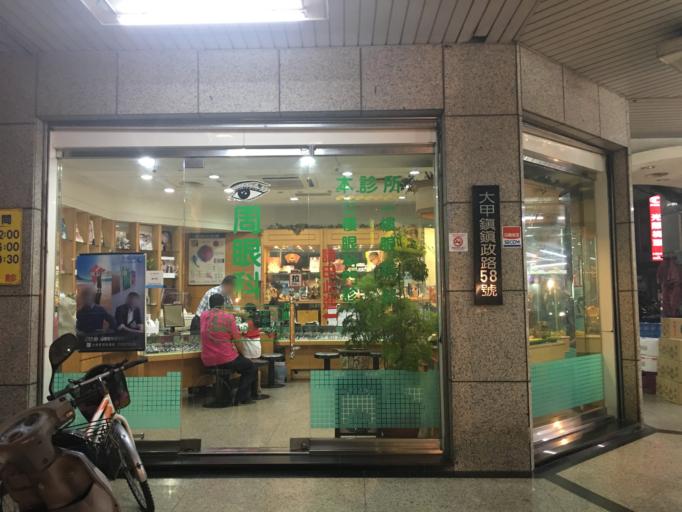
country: TW
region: Taiwan
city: Fengyuan
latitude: 24.3470
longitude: 120.6256
